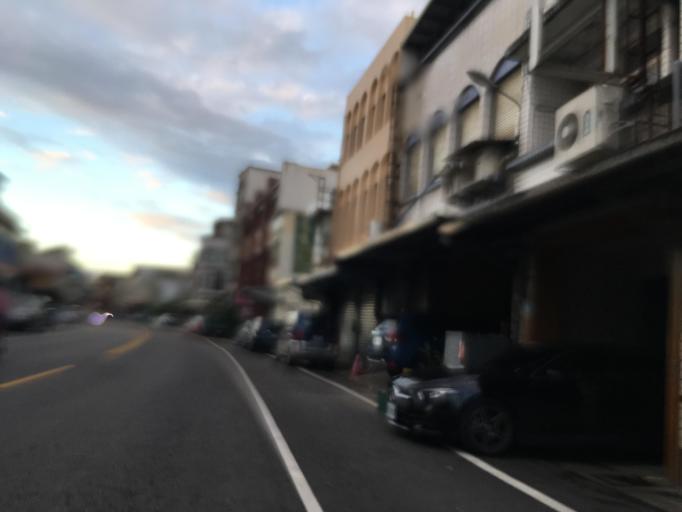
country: TW
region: Taiwan
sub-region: Yilan
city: Yilan
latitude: 24.6230
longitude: 121.8345
